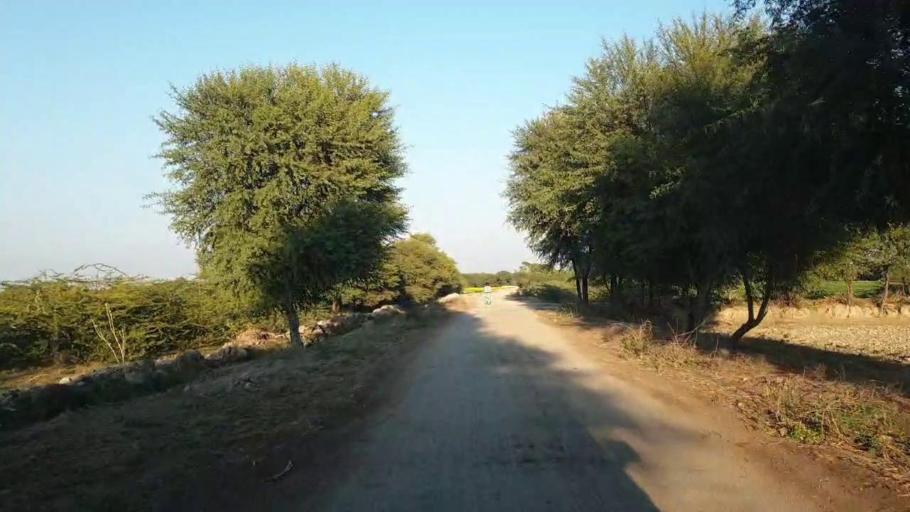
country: PK
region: Sindh
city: Shahpur Chakar
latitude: 26.1417
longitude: 68.5688
